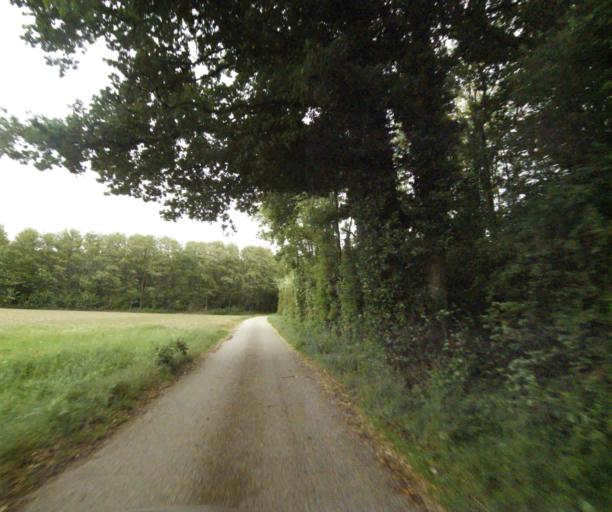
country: FR
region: Rhone-Alpes
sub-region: Departement de l'Ain
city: Mionnay
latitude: 45.8660
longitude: 4.9300
